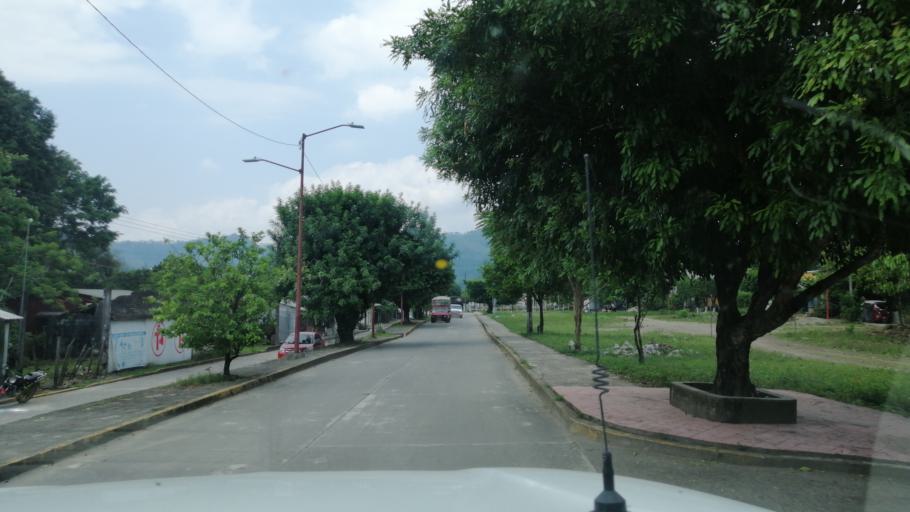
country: MX
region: Chiapas
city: Ostuacan
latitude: 17.4047
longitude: -93.3340
